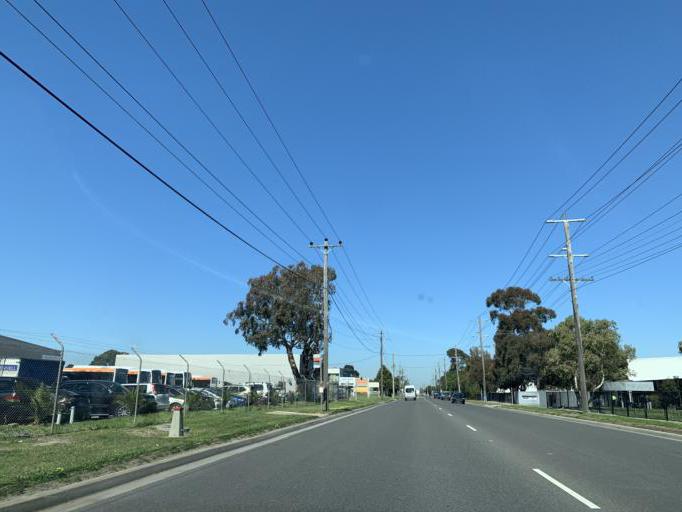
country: AU
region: Victoria
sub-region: Greater Dandenong
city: Dandenong
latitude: -38.0090
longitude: 145.2067
